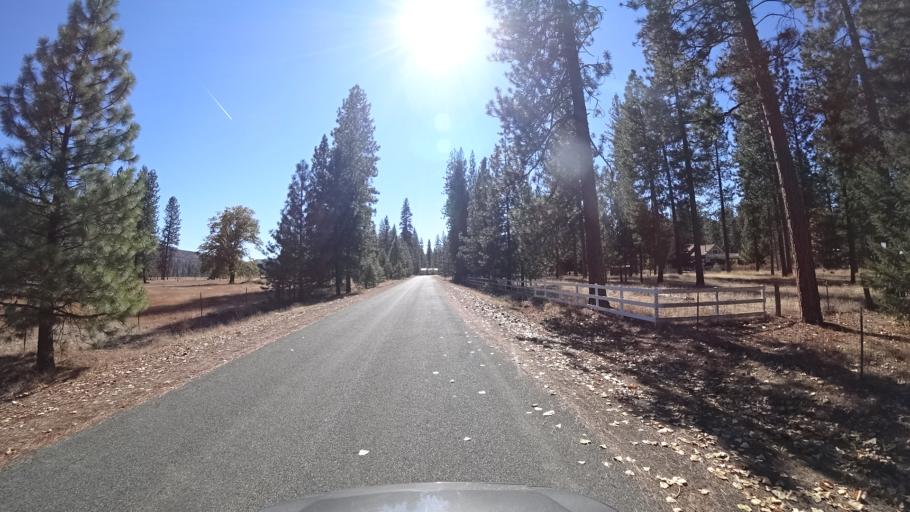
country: US
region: California
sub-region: Siskiyou County
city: Yreka
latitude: 41.6050
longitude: -122.9699
